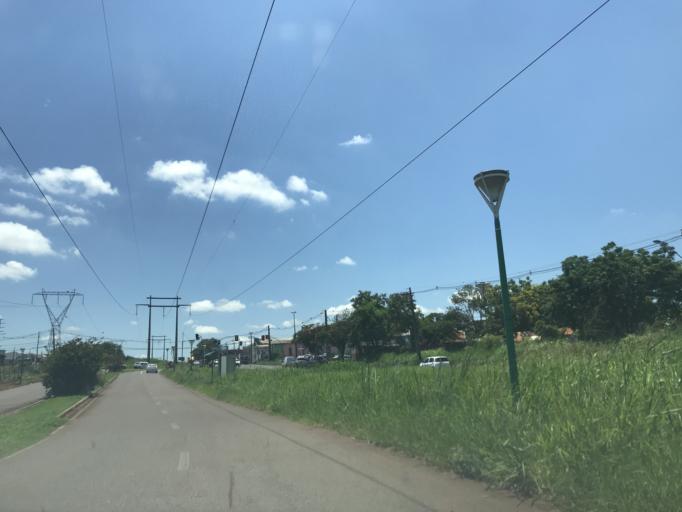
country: BR
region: Parana
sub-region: Maringa
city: Maringa
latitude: -23.4603
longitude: -51.9197
